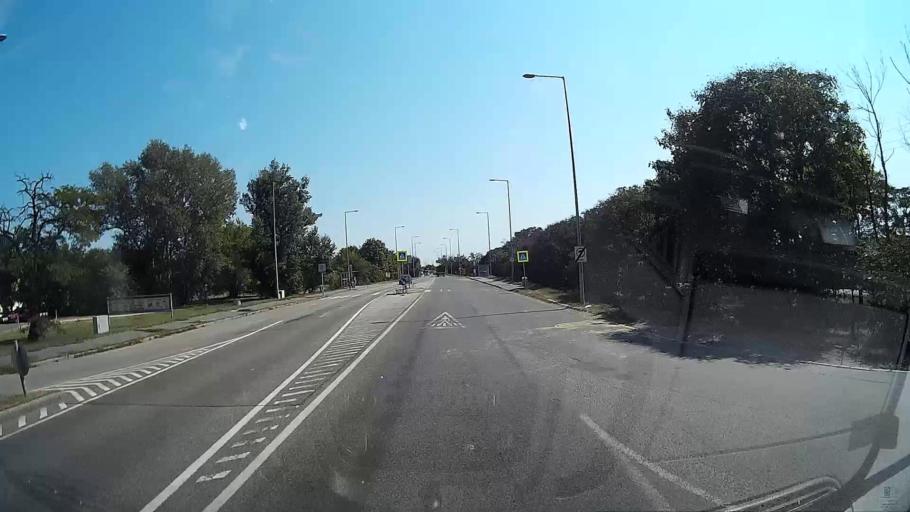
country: HU
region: Budapest
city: Budapest XXIII. keruelet
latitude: 47.3841
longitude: 19.1251
